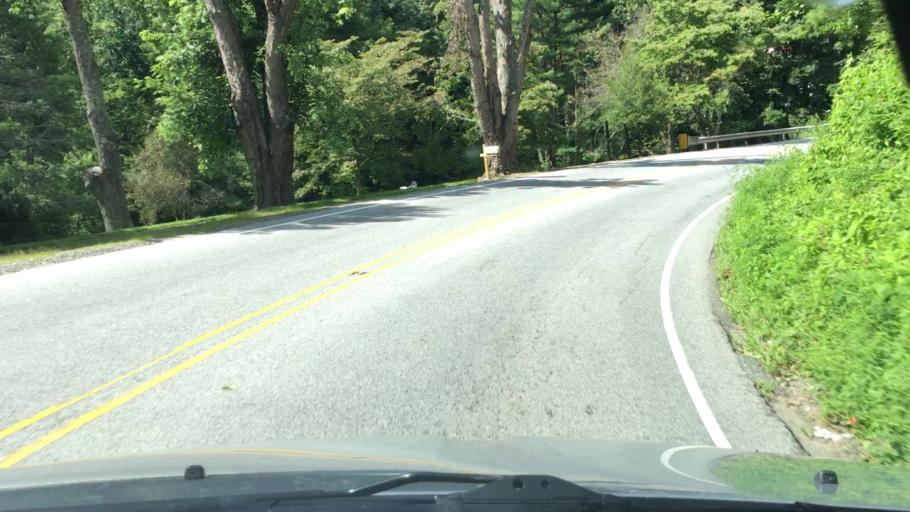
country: US
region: North Carolina
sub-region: Yancey County
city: Burnsville
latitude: 35.9011
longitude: -82.2133
